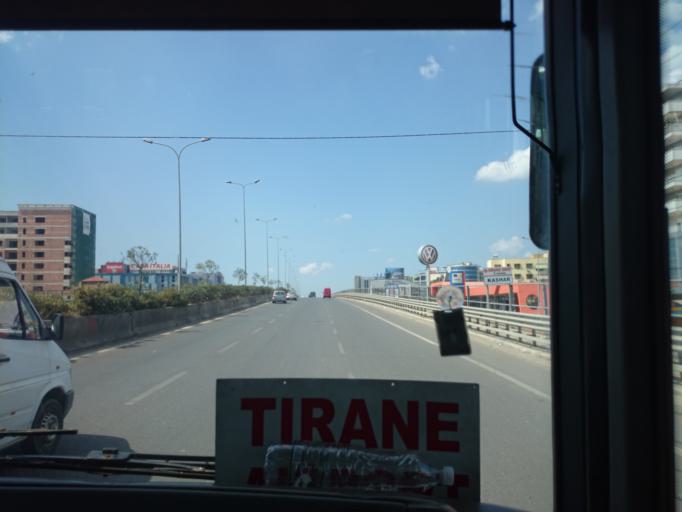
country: AL
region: Tirane
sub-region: Rrethi i Tiranes
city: Paskuqan
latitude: 41.3418
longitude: 19.7795
